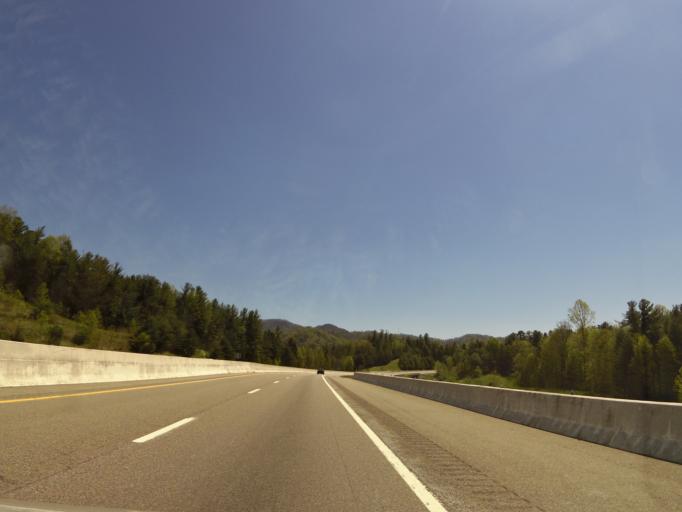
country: US
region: Tennessee
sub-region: Unicoi County
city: Banner Hill
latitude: 36.0525
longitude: -82.5135
